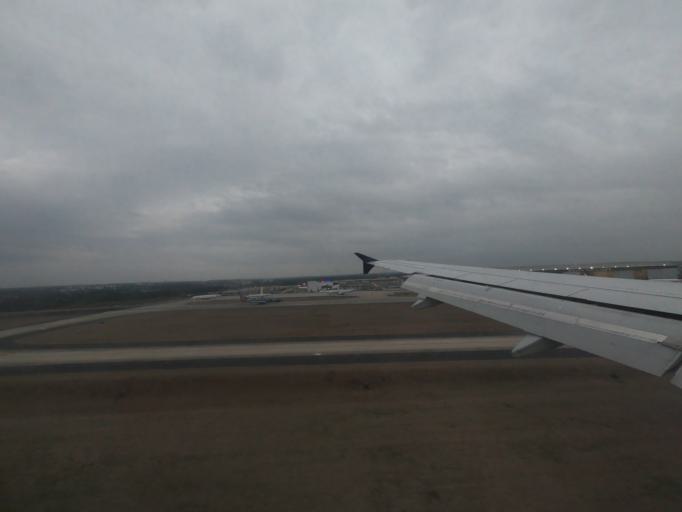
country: US
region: Georgia
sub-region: Fulton County
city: Hapeville
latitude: 33.6496
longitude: -84.4079
